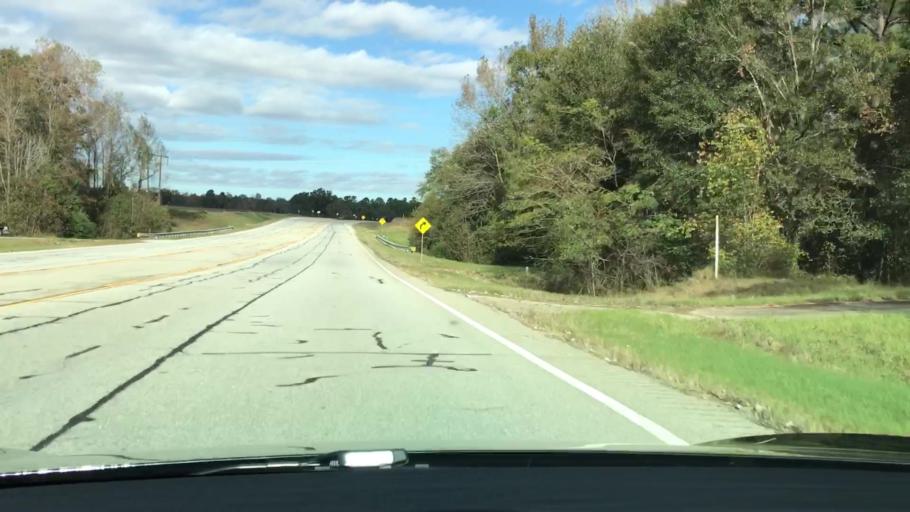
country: US
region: Georgia
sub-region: Jefferson County
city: Wadley
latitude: 32.8870
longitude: -82.3973
